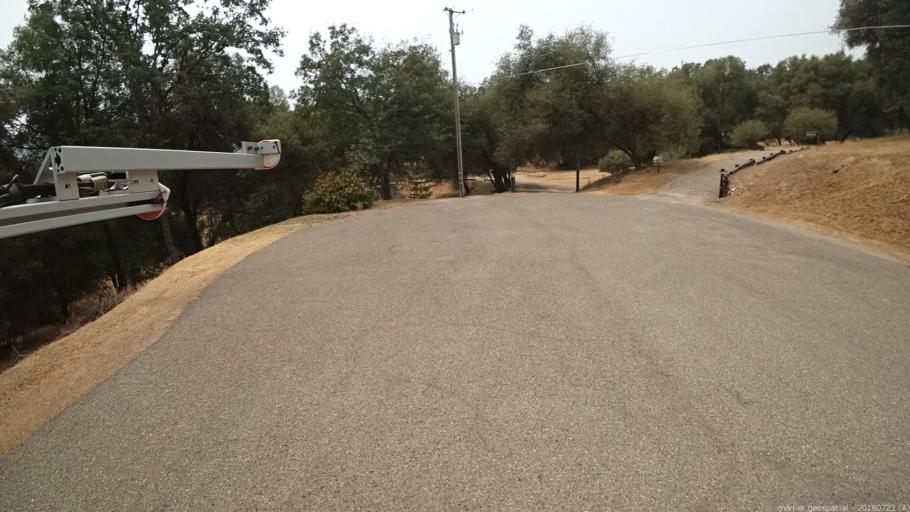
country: US
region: California
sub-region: Madera County
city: Oakhurst
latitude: 37.3390
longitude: -119.6486
